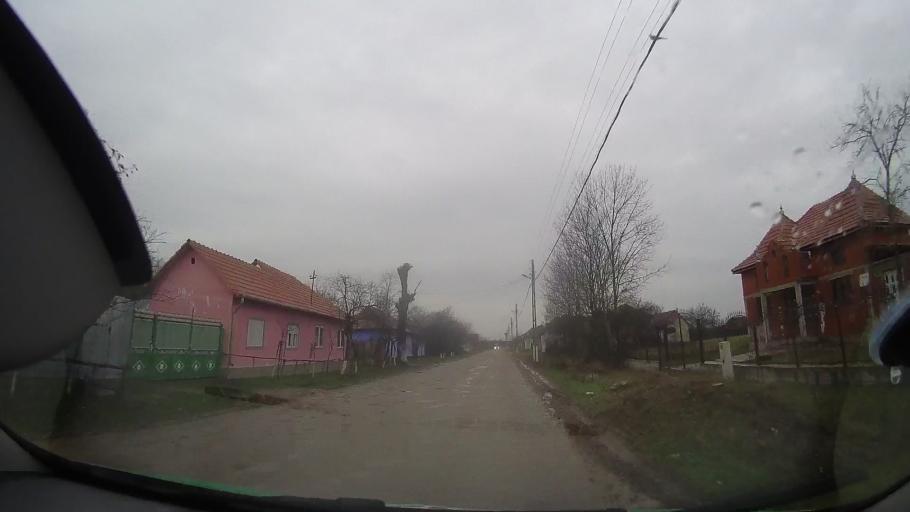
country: RO
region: Bihor
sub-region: Comuna Olcea
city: Olcea
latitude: 46.6869
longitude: 21.9964
